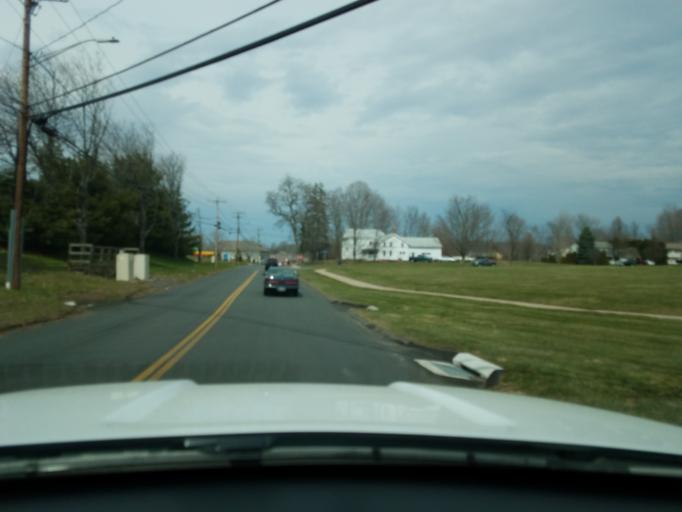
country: US
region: Connecticut
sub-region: Hartford County
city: Newington
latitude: 41.6629
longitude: -72.7173
